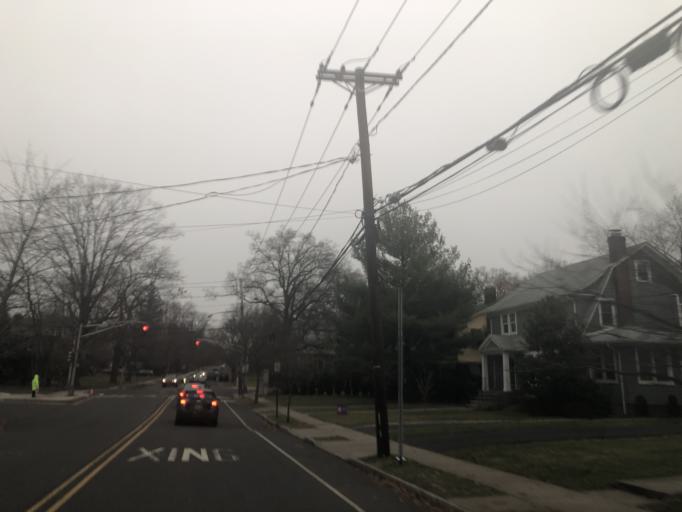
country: US
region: New Jersey
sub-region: Essex County
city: Maplewood
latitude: 40.7252
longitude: -74.2701
